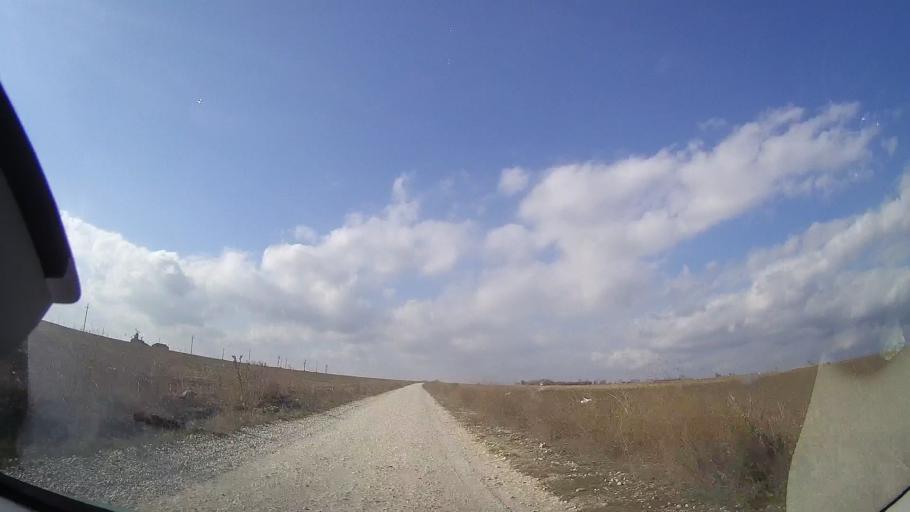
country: RO
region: Constanta
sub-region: Comuna Douazeci si Trei August
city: Douazeci si Trei August
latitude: 43.9102
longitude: 28.6026
